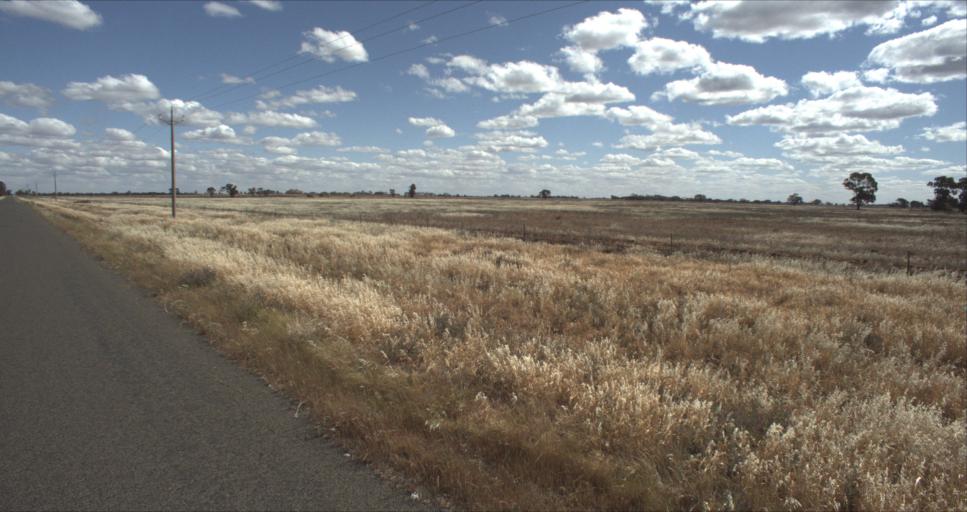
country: AU
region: New South Wales
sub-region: Leeton
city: Leeton
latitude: -34.4663
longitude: 146.2517
